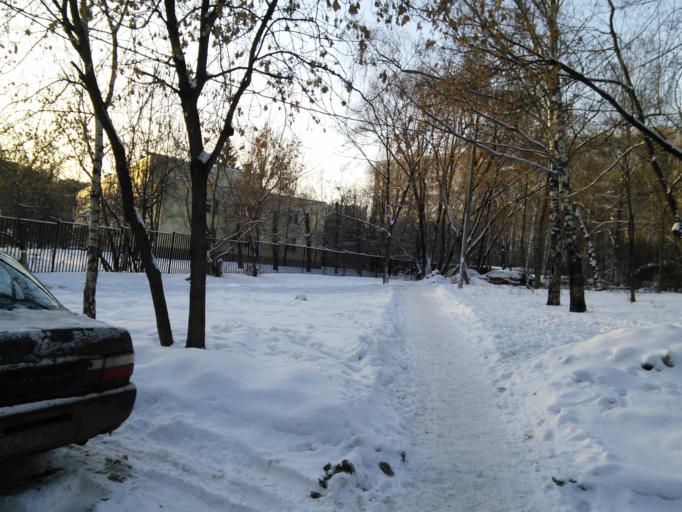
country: RU
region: Moscow
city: Davydkovo
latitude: 55.7234
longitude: 37.4760
